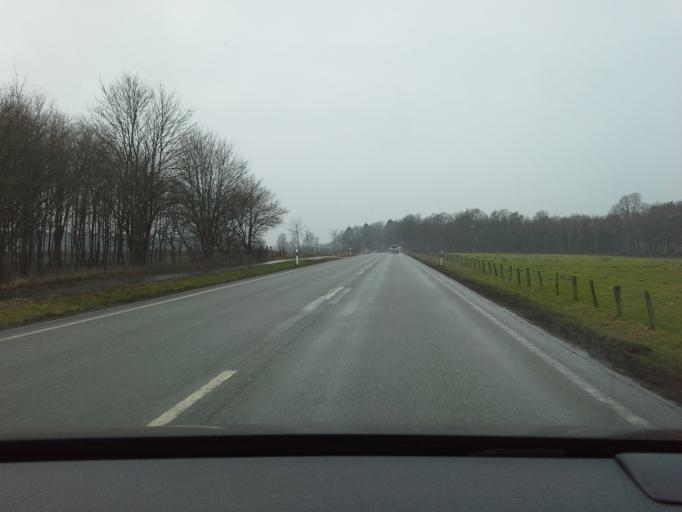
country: DE
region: Schleswig-Holstein
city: Appen
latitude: 53.6301
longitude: 9.7271
